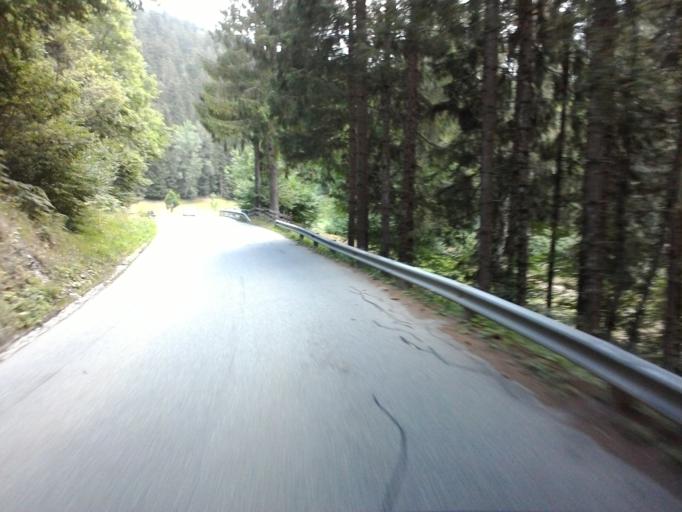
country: AT
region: Carinthia
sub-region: Politischer Bezirk Spittal an der Drau
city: Oberdrauburg
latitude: 46.6801
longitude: 12.9605
